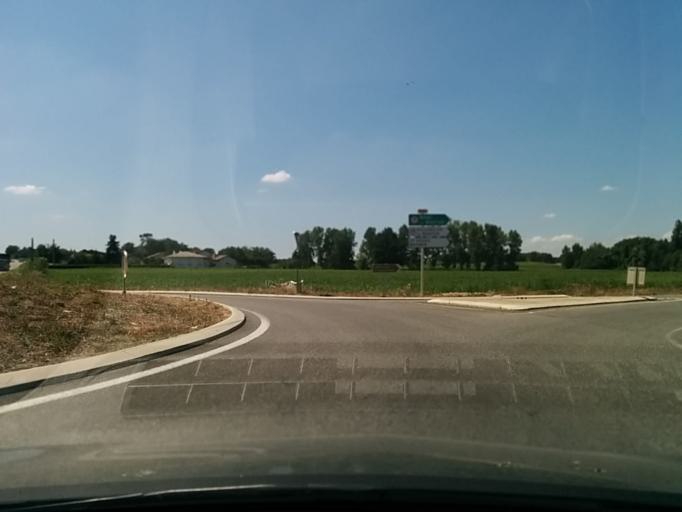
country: FR
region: Midi-Pyrenees
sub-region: Departement du Gers
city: Nogaro
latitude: 43.7509
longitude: -0.0913
